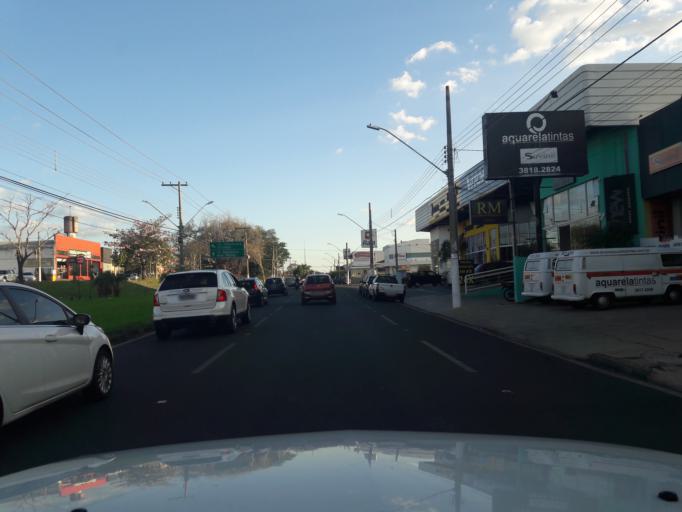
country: BR
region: Sao Paulo
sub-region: Moji-Guacu
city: Mogi-Gaucu
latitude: -22.3903
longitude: -46.9451
